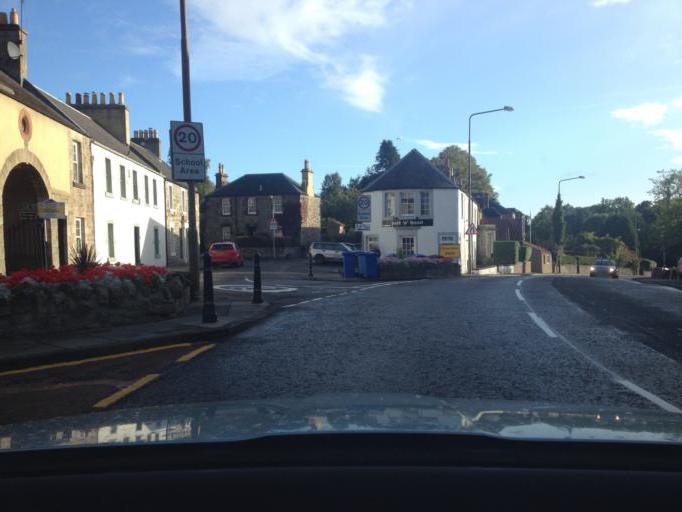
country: GB
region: Scotland
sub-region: West Lothian
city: Mid Calder
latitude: 55.8927
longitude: -3.4802
